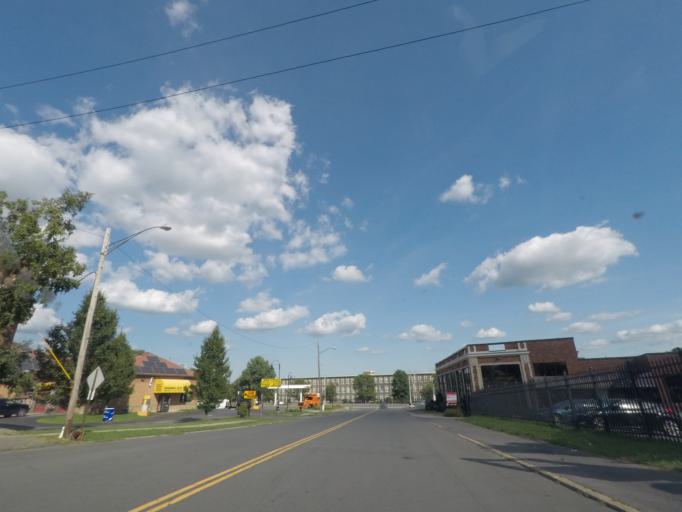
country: US
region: New York
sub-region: Albany County
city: Menands
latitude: 42.6775
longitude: -73.7364
